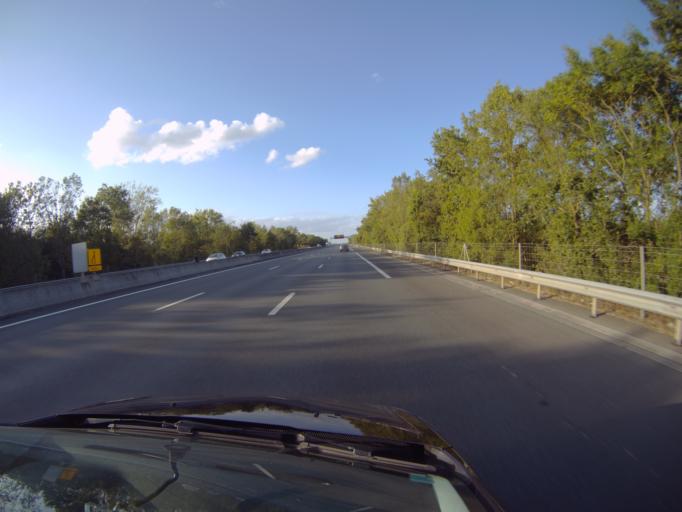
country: FR
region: Pays de la Loire
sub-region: Departement de Maine-et-Loire
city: Les Ponts-de-Ce
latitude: 47.4076
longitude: -0.5089
